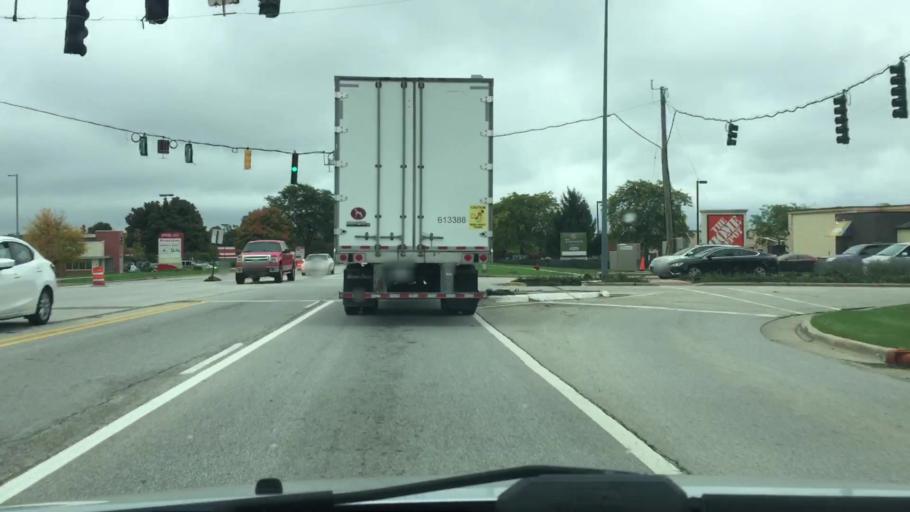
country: US
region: Illinois
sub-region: Kane County
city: West Dundee
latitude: 42.1064
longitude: -88.2924
